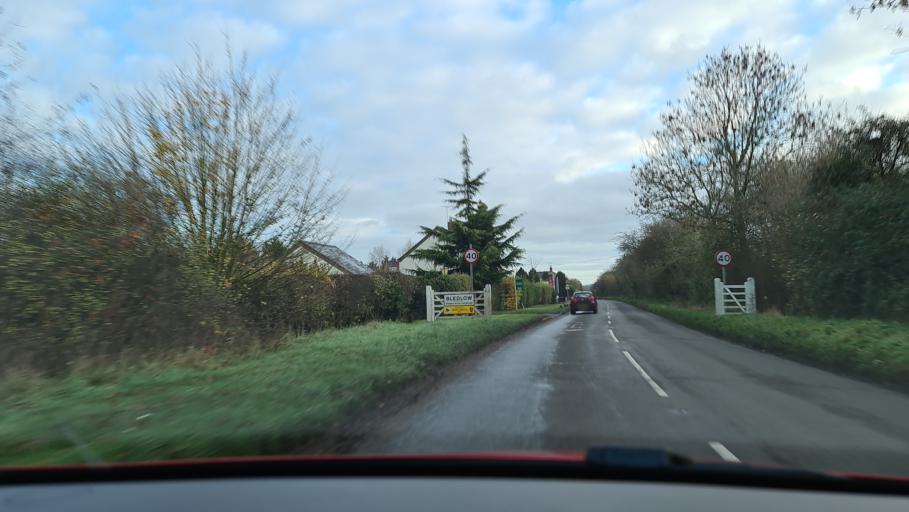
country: GB
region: England
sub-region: Oxfordshire
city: Chinnor
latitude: 51.7160
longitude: -0.8855
